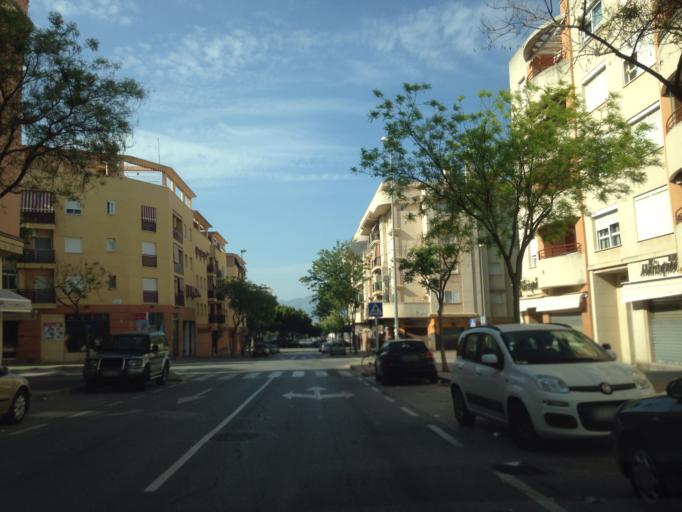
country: ES
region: Andalusia
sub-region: Provincia de Malaga
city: Malaga
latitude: 36.7226
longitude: -4.4771
